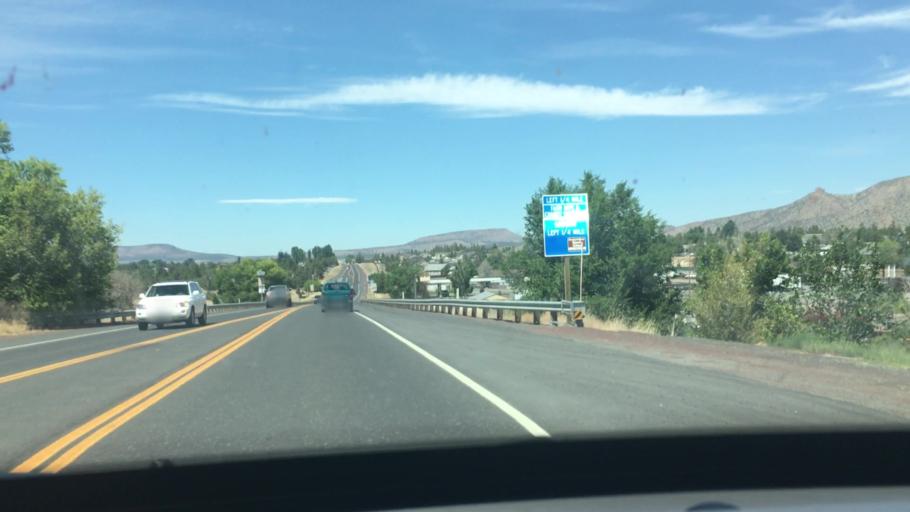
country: US
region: Oregon
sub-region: Deschutes County
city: Terrebonne
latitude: 44.3546
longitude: -121.1787
